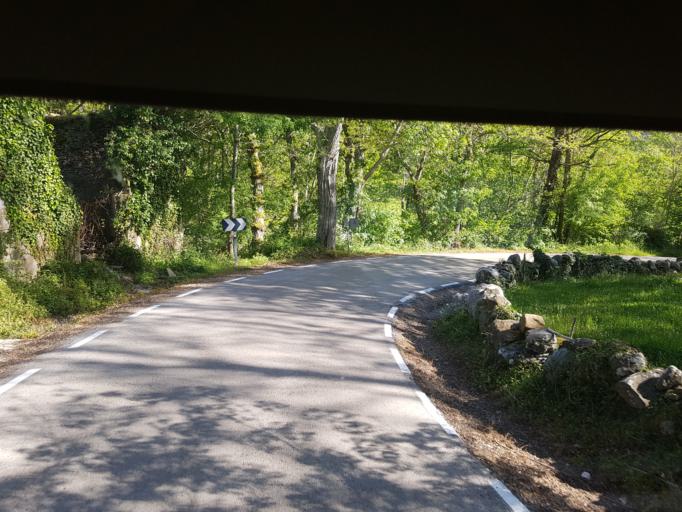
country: ES
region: Castille and Leon
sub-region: Provincia de Burgos
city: Espinosa de los Monteros
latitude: 43.1207
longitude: -3.5794
